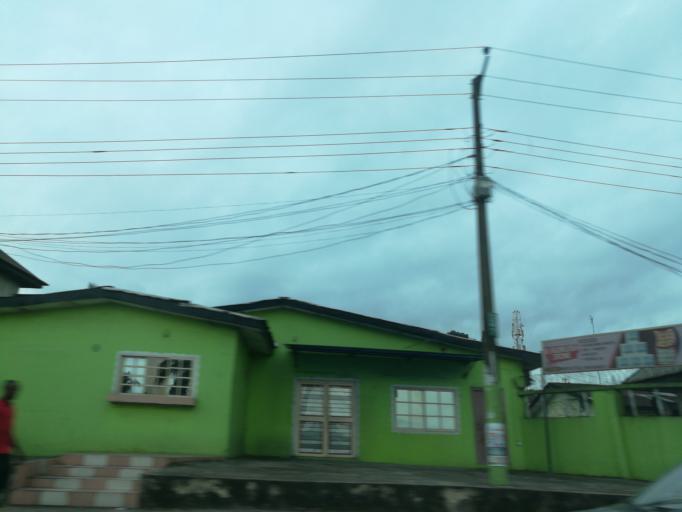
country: NG
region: Rivers
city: Port Harcourt
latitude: 4.8185
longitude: 7.0236
